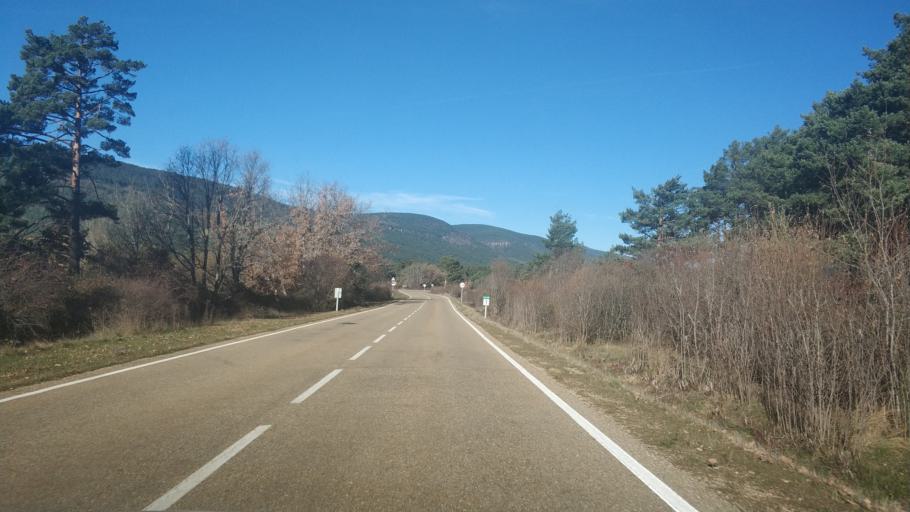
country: ES
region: Castille and Leon
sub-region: Provincia de Soria
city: Vinuesa
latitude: 41.9196
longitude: -2.7579
